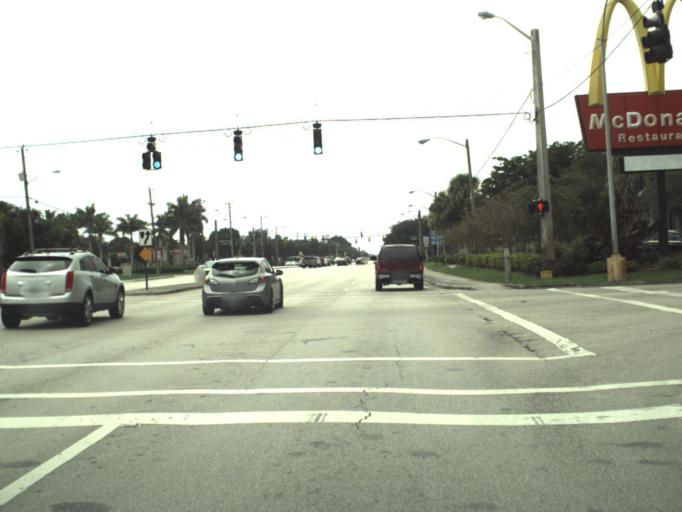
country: US
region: Florida
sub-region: Palm Beach County
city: Kings Point
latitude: 26.4600
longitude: -80.1227
